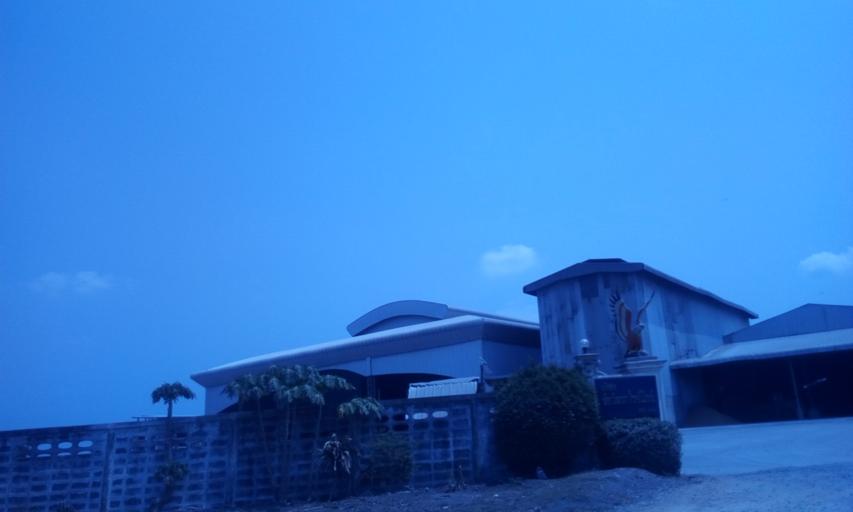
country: TH
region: Chachoengsao
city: Bang Nam Priao
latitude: 13.9529
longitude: 100.9727
